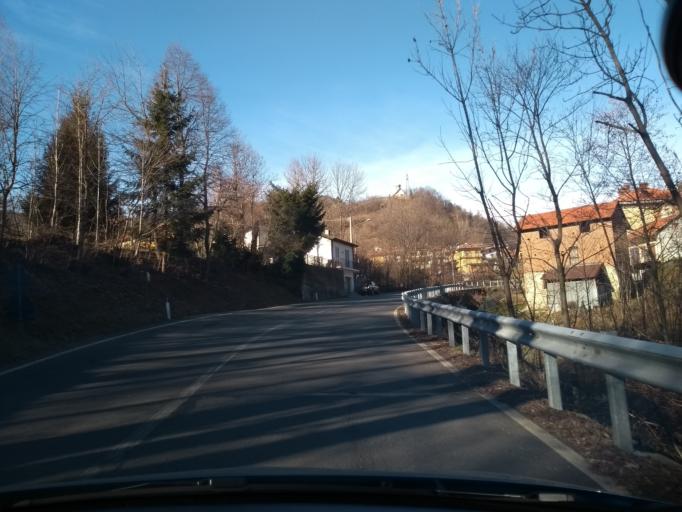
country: IT
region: Piedmont
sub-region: Provincia di Torino
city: Germagnano
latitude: 45.2638
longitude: 7.4538
